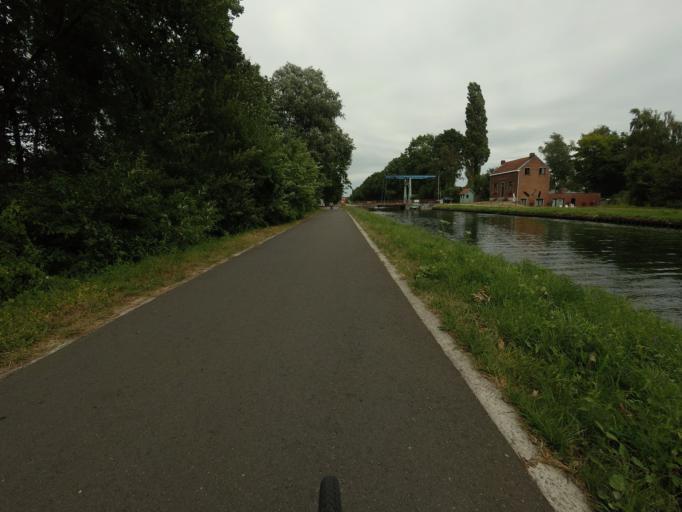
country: BE
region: Flanders
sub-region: Provincie Antwerpen
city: Schoten
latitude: 51.2611
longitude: 4.5115
